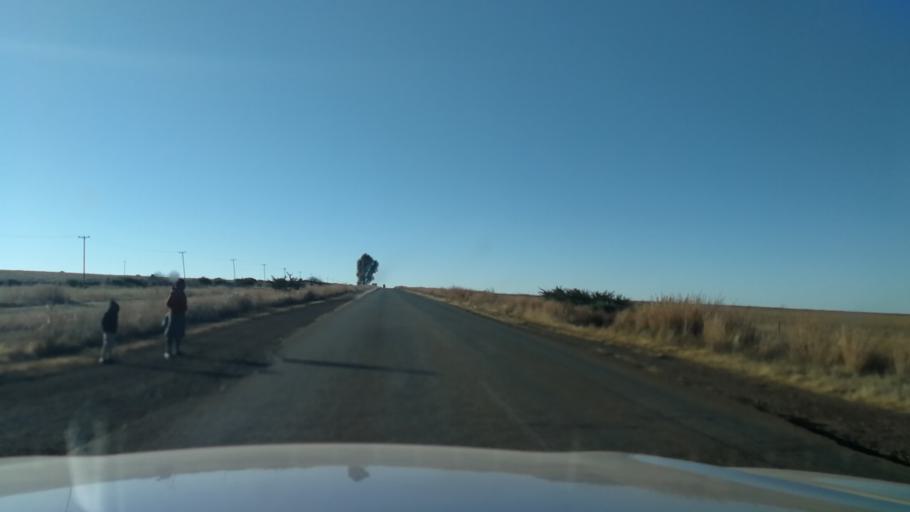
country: ZA
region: North-West
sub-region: Bojanala Platinum District Municipality
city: Rustenburg
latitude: -25.9623
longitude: 27.2087
